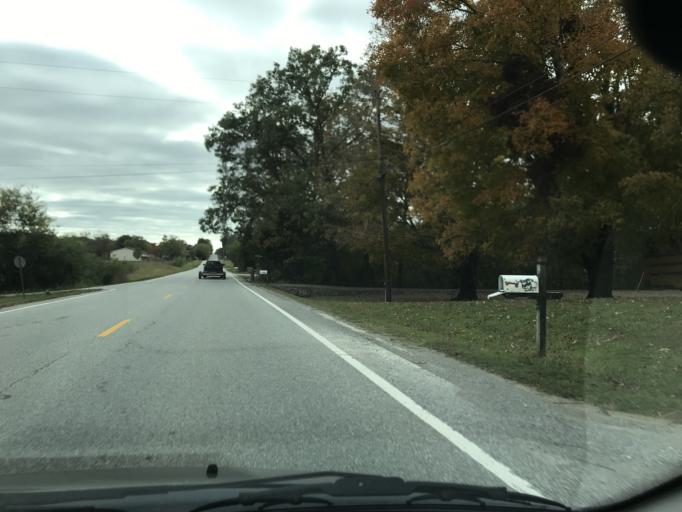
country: US
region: Tennessee
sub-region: Hamilton County
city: Lakesite
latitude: 35.2369
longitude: -85.0143
